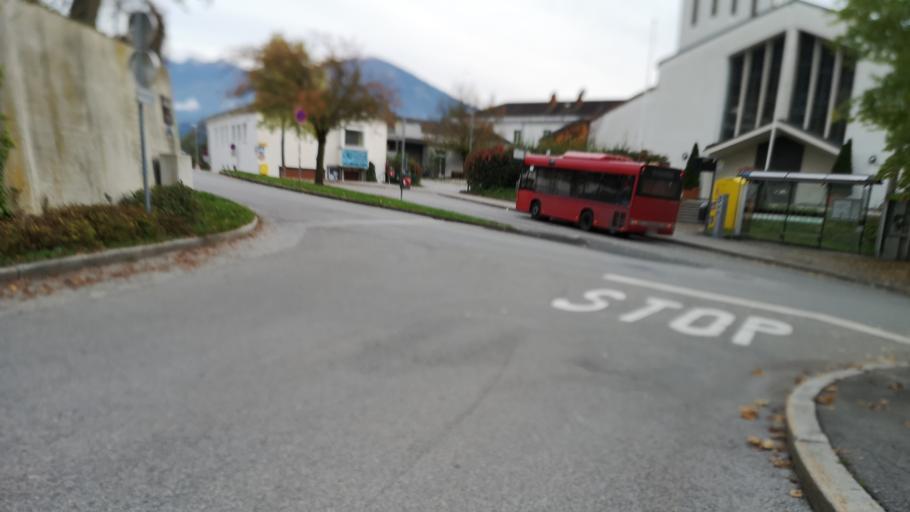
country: AT
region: Tyrol
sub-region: Politischer Bezirk Innsbruck Land
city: Vols
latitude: 47.2686
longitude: 11.3552
